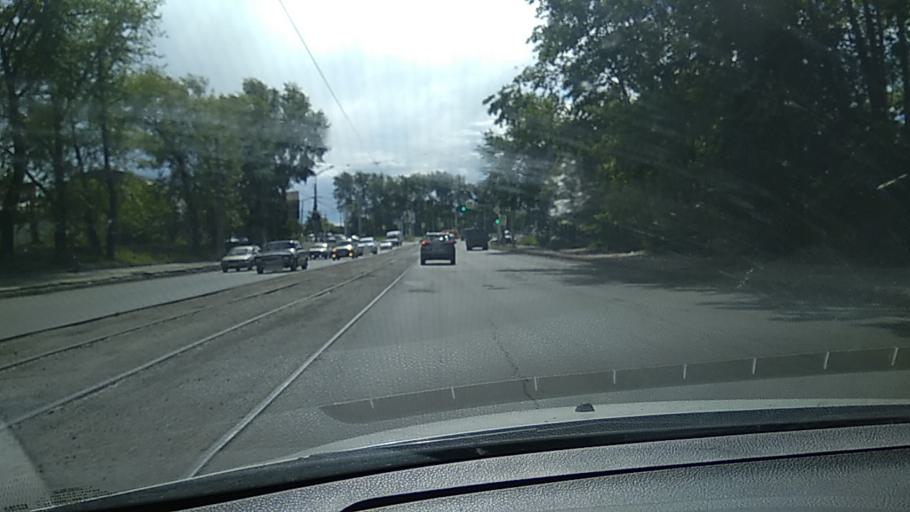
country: RU
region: Sverdlovsk
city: Nizhniy Tagil
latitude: 57.9230
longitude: 59.9892
